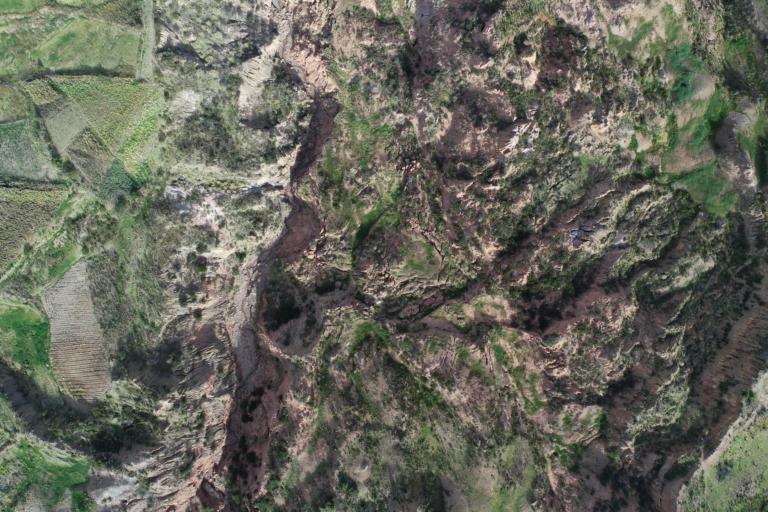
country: BO
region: La Paz
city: La Paz
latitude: -16.5538
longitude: -67.9927
